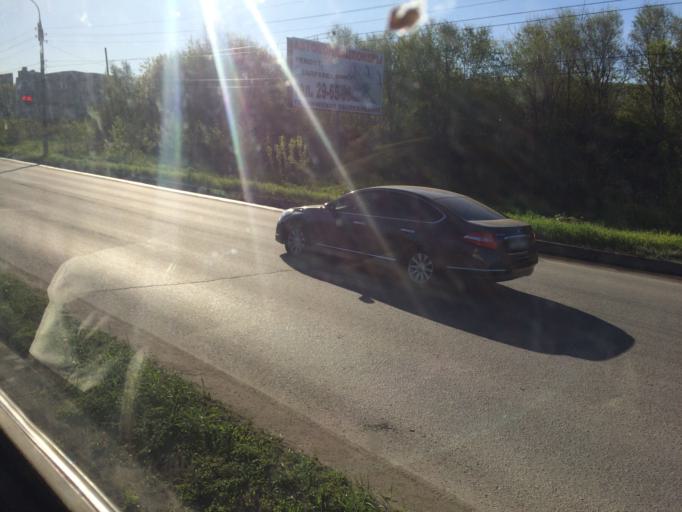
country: RU
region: Chelyabinsk
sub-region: Gorod Magnitogorsk
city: Magnitogorsk
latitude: 53.3972
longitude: 59.0320
